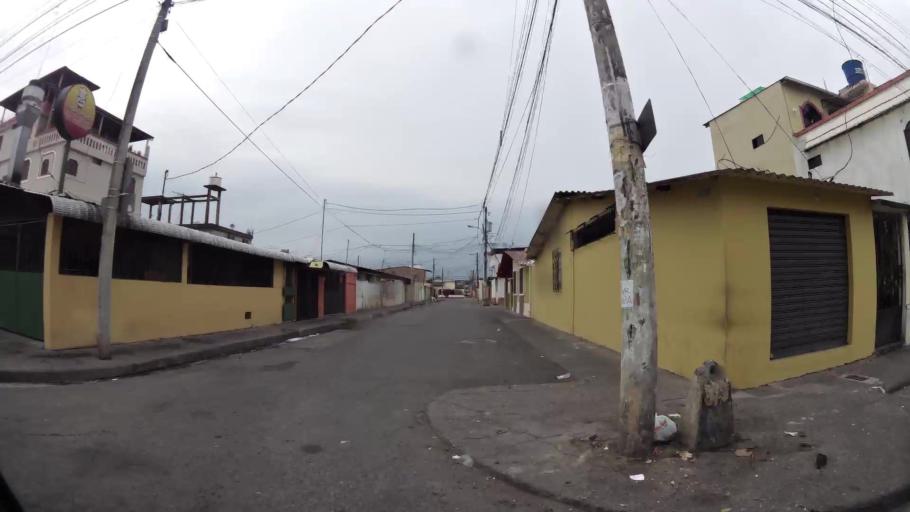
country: EC
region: Guayas
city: Eloy Alfaro
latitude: -2.1400
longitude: -79.9035
